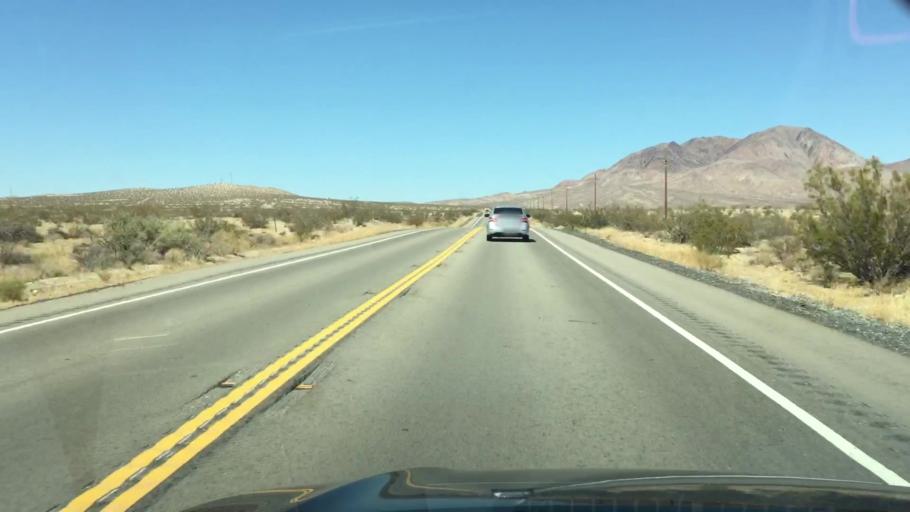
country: US
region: California
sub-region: Kern County
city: Boron
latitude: 35.2974
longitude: -117.6141
